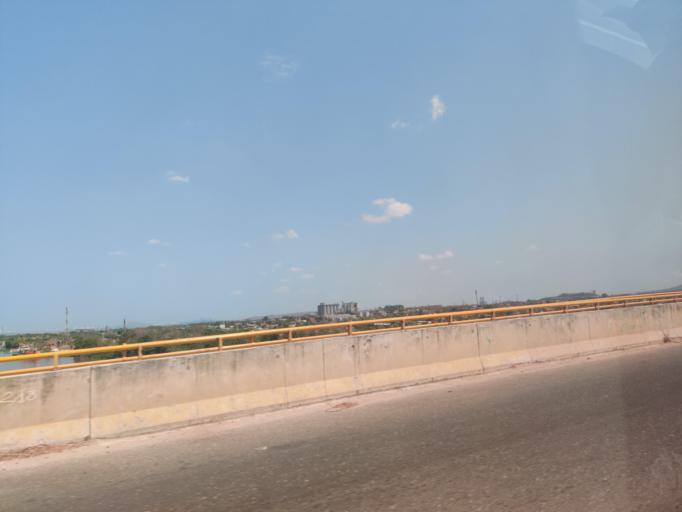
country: CO
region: Bolivar
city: Turbana
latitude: 10.2763
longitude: -75.5190
